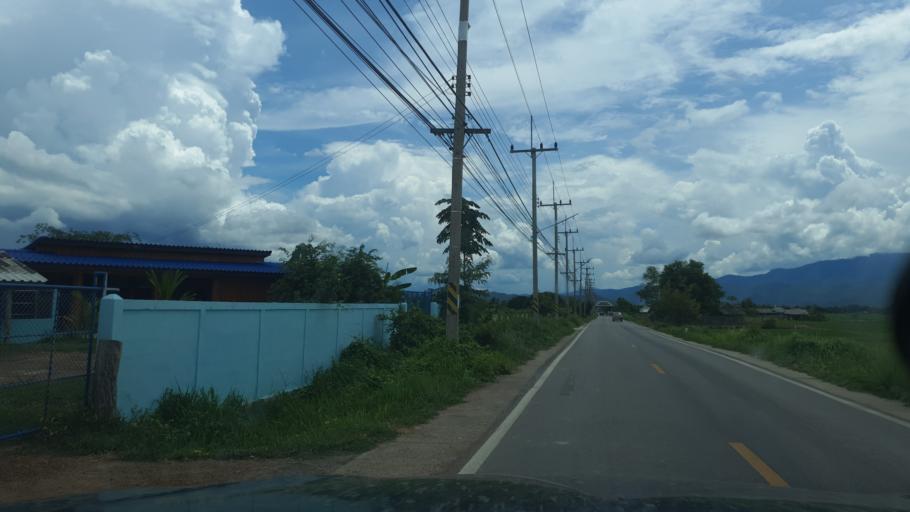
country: TH
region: Lampang
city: Sop Prap
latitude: 17.8794
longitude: 99.3707
